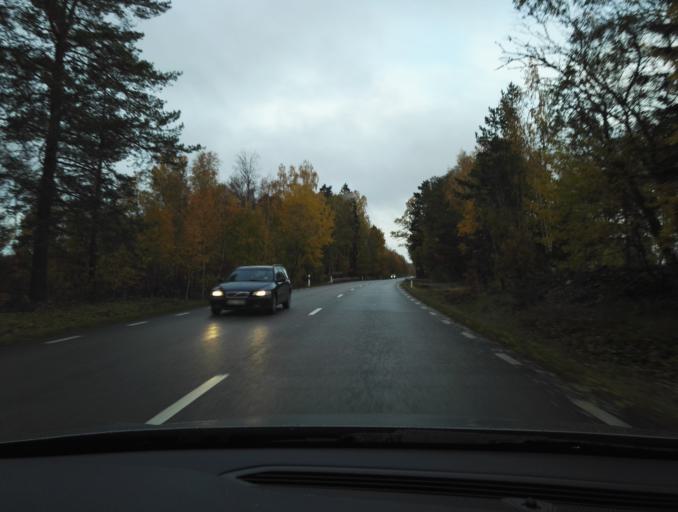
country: SE
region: Kronoberg
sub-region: Vaxjo Kommun
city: Gemla
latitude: 56.9569
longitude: 14.7157
